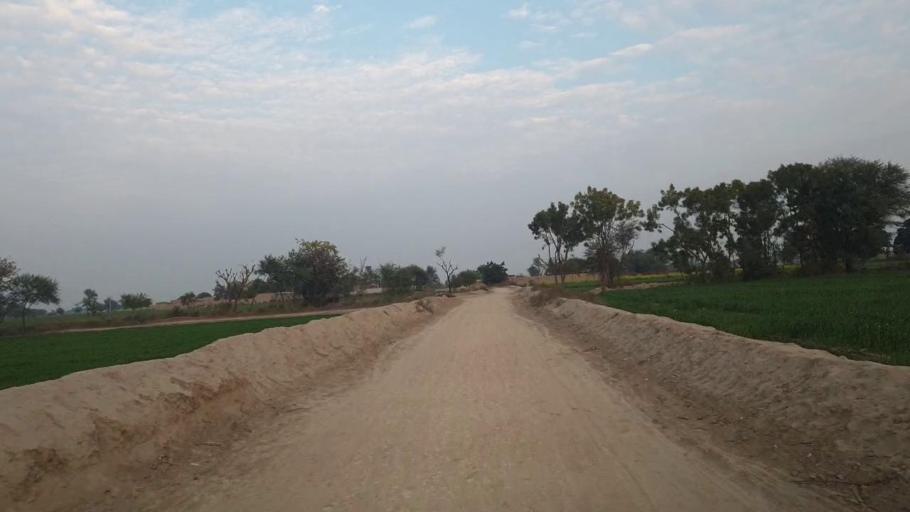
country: PK
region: Sindh
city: Shahpur Chakar
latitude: 26.0875
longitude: 68.5528
